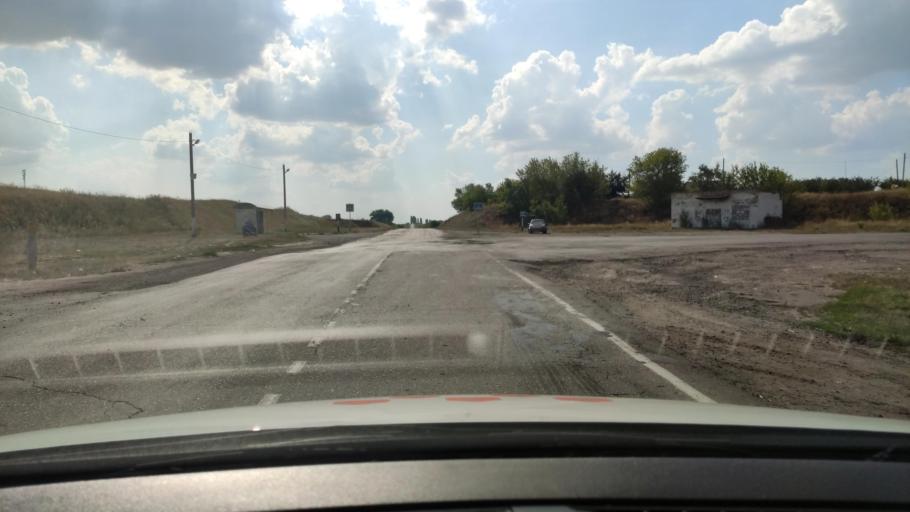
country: RU
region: Voronezj
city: Sadovoye
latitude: 51.7685
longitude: 40.4869
